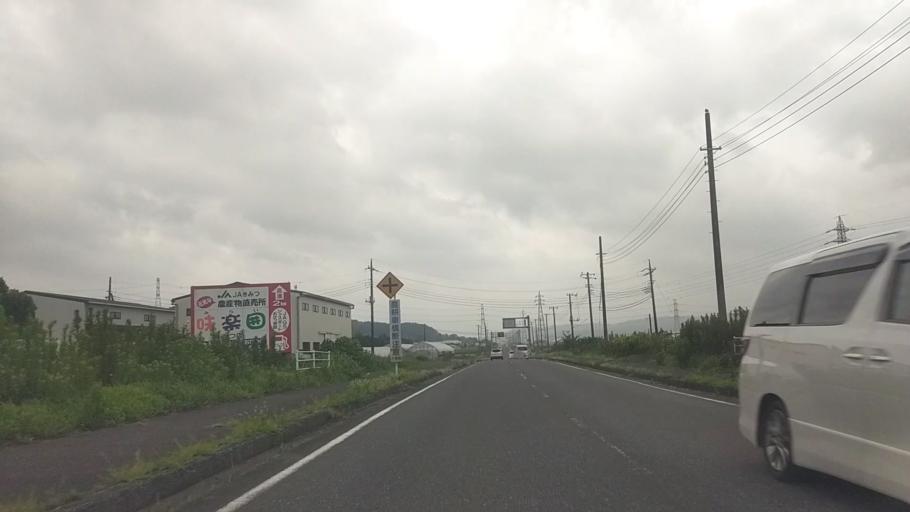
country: JP
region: Chiba
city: Kisarazu
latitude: 35.3546
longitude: 140.0548
